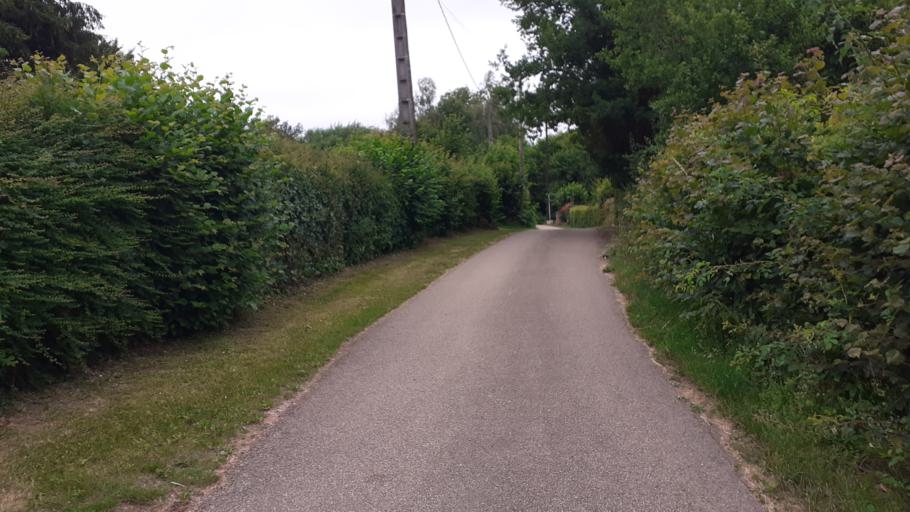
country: FR
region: Bourgogne
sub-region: Departement de la Cote-d'Or
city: Saulieu
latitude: 47.2707
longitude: 4.1402
